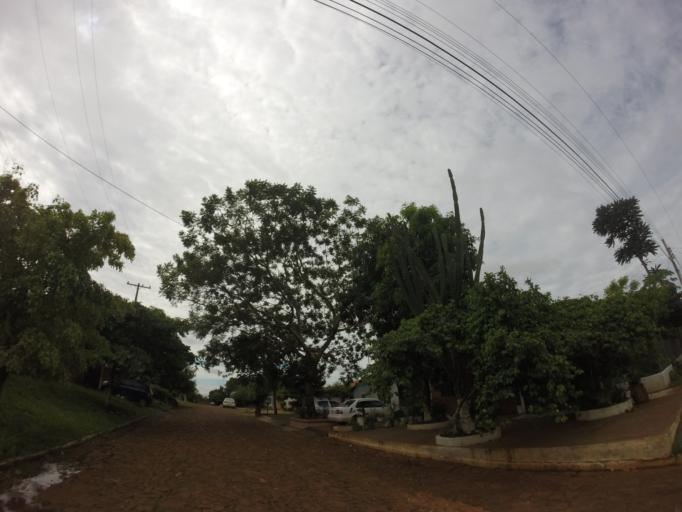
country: PY
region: Alto Parana
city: Ciudad del Este
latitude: -25.4080
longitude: -54.6490
